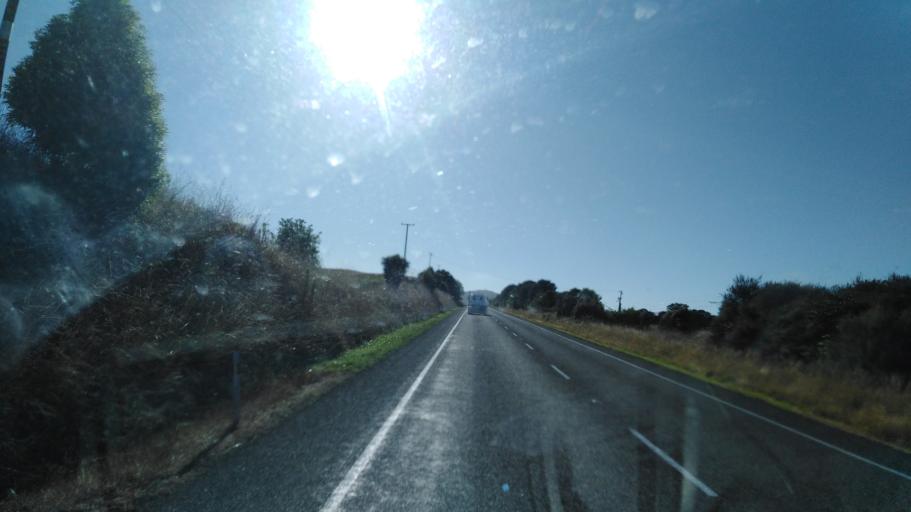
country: NZ
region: Manawatu-Wanganui
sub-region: Ruapehu District
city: Waiouru
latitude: -39.8386
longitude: 175.7549
